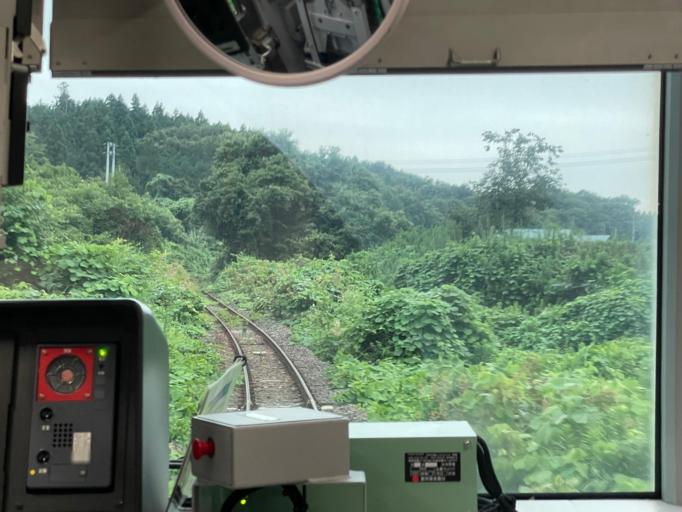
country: JP
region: Tochigi
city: Karasuyama
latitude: 36.6673
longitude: 140.0649
